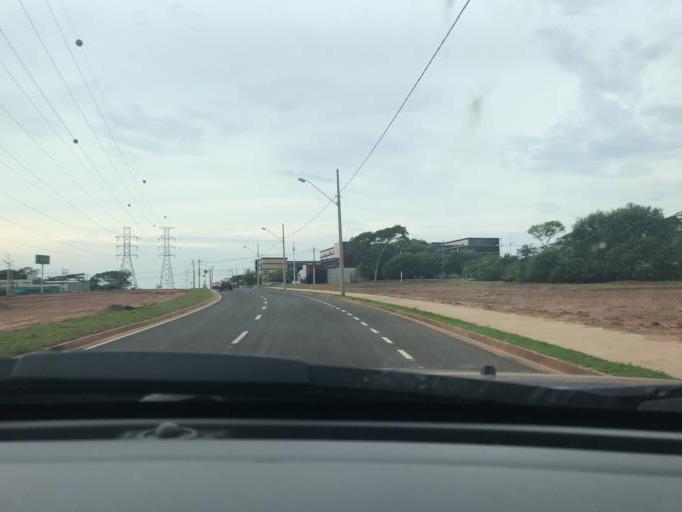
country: BR
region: Sao Paulo
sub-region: Sao Jose Do Rio Preto
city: Sao Jose do Rio Preto
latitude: -20.8448
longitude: -49.4044
